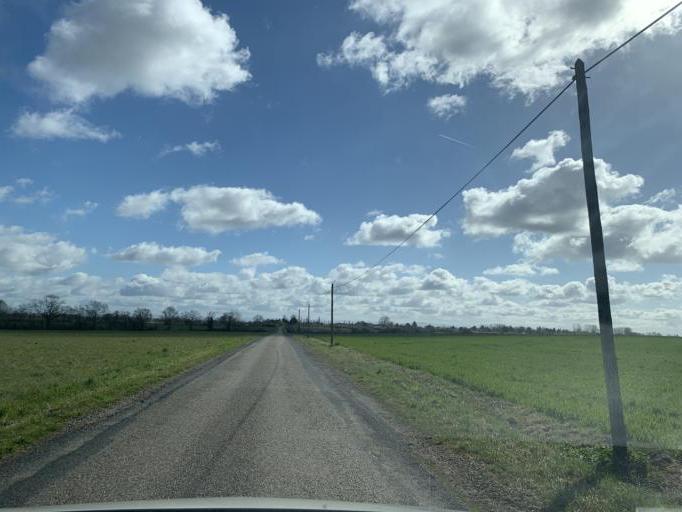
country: FR
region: Rhone-Alpes
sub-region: Departement de l'Ain
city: Saint-Andre-de-Corcy
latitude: 45.9504
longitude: 4.9676
